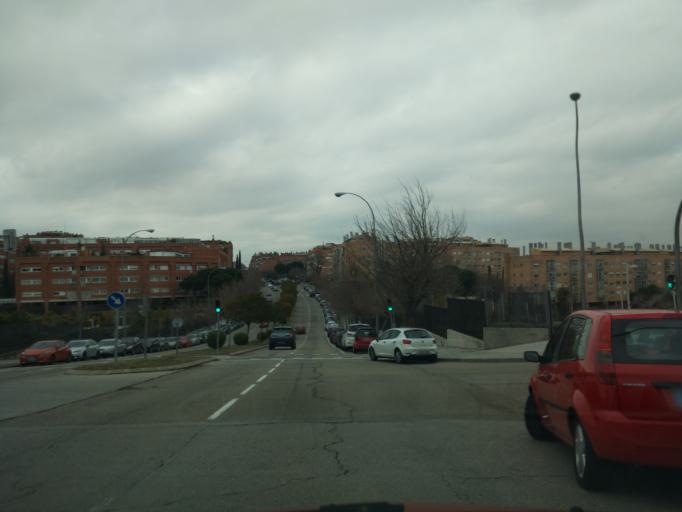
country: ES
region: Madrid
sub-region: Provincia de Madrid
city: San Blas
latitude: 40.4552
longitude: -3.6231
